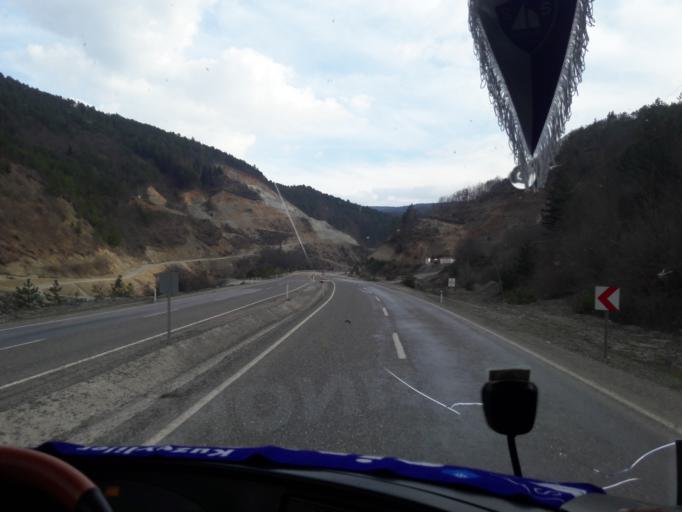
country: TR
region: Kastamonu
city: Kuzyaka
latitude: 41.1876
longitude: 33.7950
